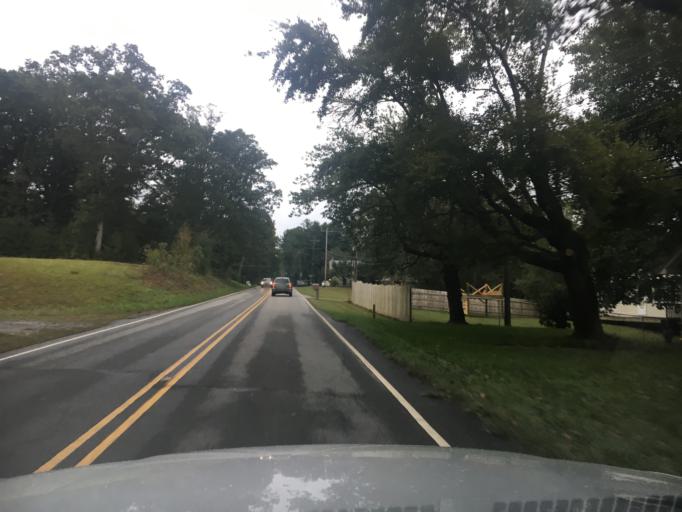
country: US
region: North Carolina
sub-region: Henderson County
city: Horse Shoe
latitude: 35.3407
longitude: -82.5401
